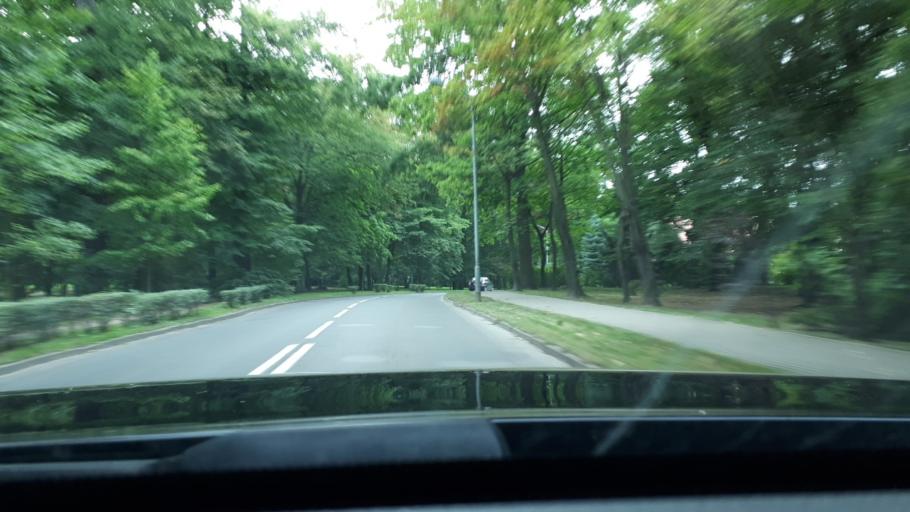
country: PL
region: Lower Silesian Voivodeship
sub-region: Powiat olesnicki
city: Olesnica
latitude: 51.2067
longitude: 17.3754
